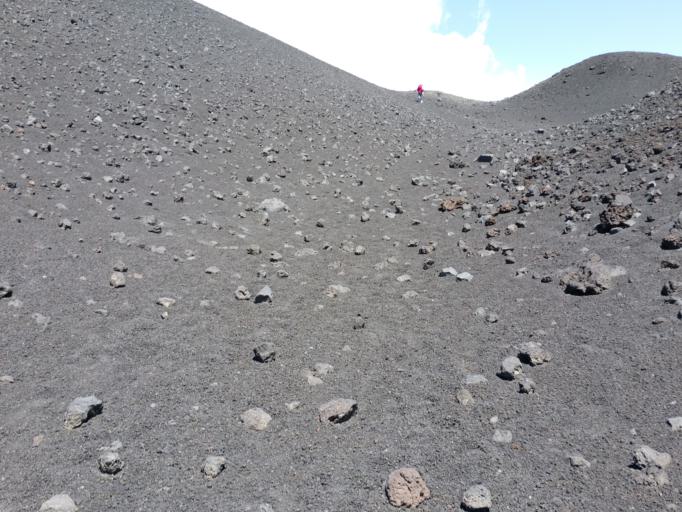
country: IT
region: Sicily
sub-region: Catania
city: Nicolosi
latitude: 37.7208
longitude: 15.0039
